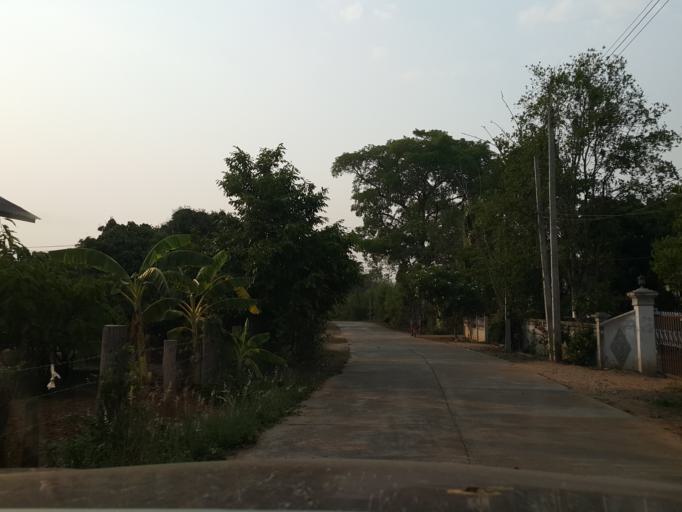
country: TH
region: Lamphun
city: Li
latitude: 17.8085
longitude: 98.9491
